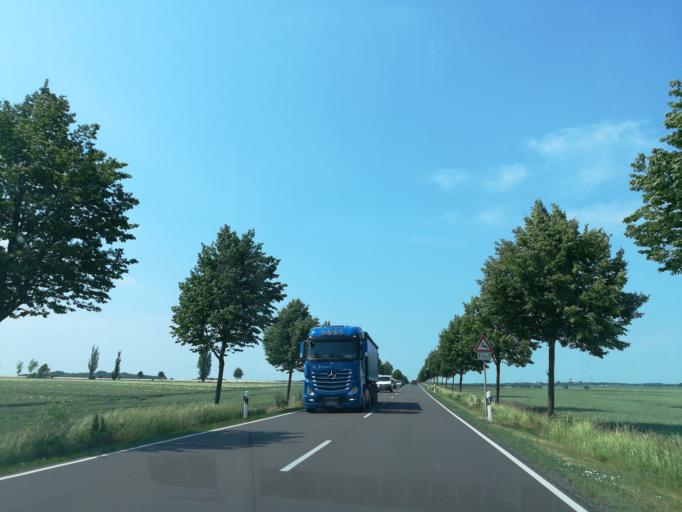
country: DE
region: Saxony-Anhalt
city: Schneidlingen
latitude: 51.9072
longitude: 11.4333
